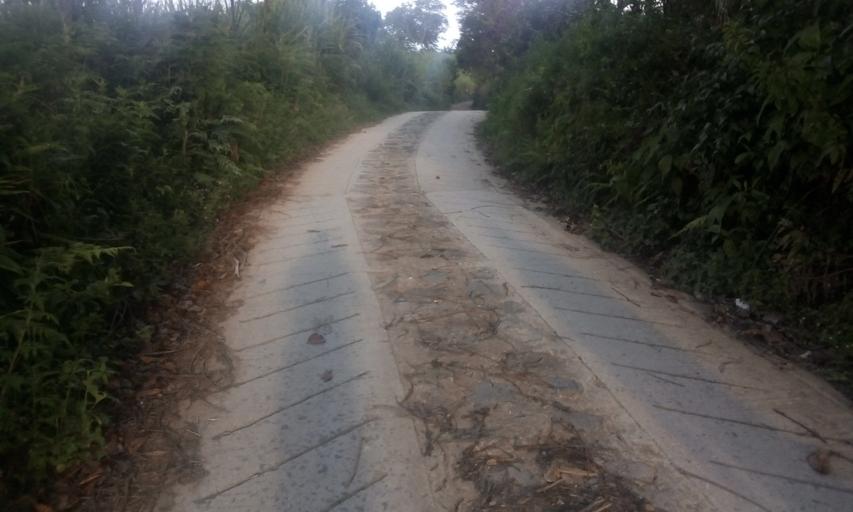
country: CO
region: Boyaca
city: Santana
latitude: 6.0044
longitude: -73.5055
